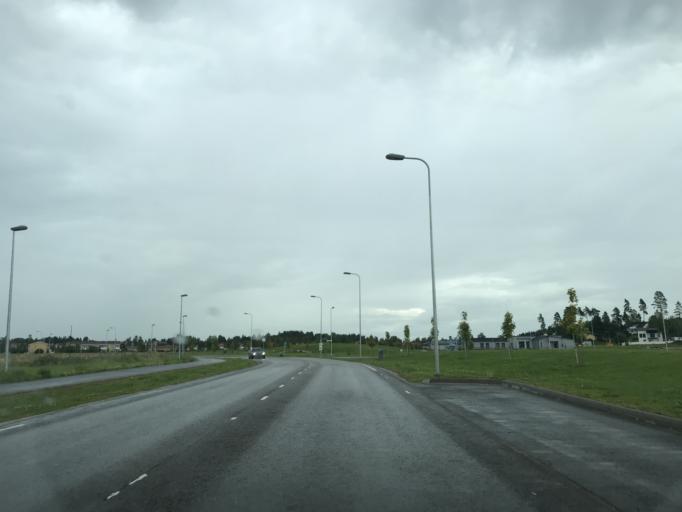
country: FI
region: Uusimaa
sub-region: Helsinki
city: Vihti
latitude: 60.3208
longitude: 24.3146
